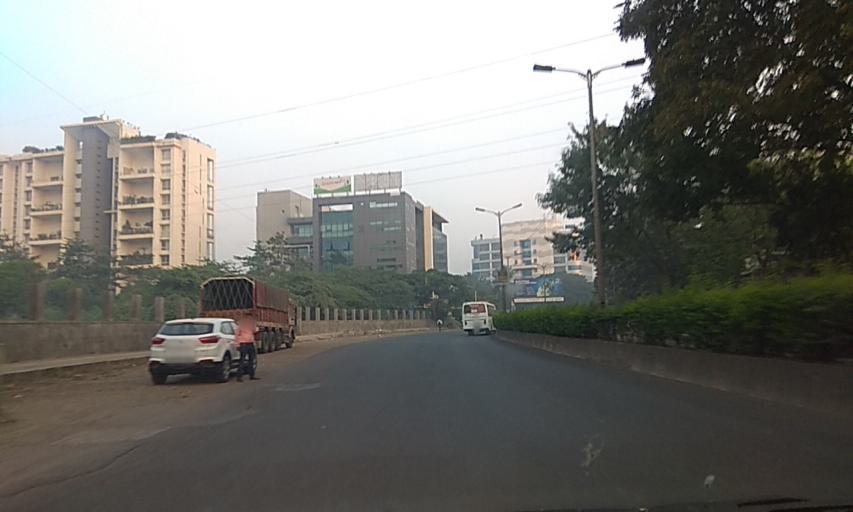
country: IN
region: Maharashtra
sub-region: Pune Division
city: Pune
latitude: 18.5210
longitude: 73.9322
